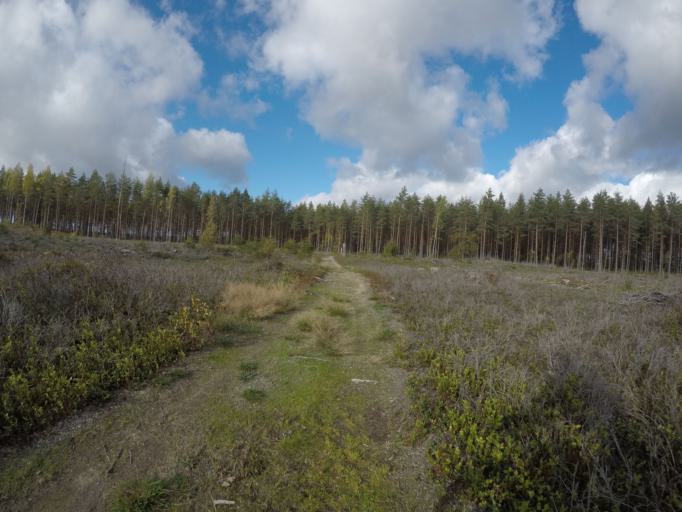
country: SE
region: Vaestmanland
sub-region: Kungsors Kommun
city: Kungsoer
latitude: 59.3042
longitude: 16.1119
